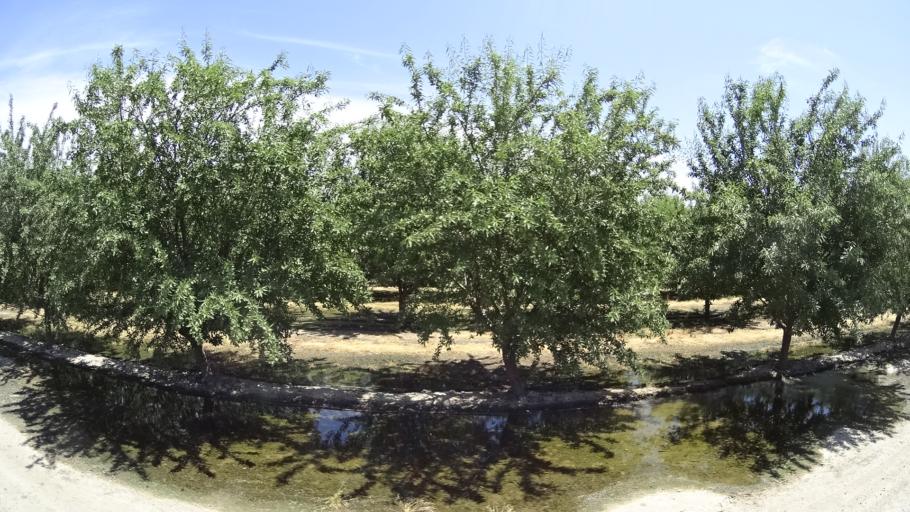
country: US
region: California
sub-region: Kings County
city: Lemoore
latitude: 36.3505
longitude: -119.7673
